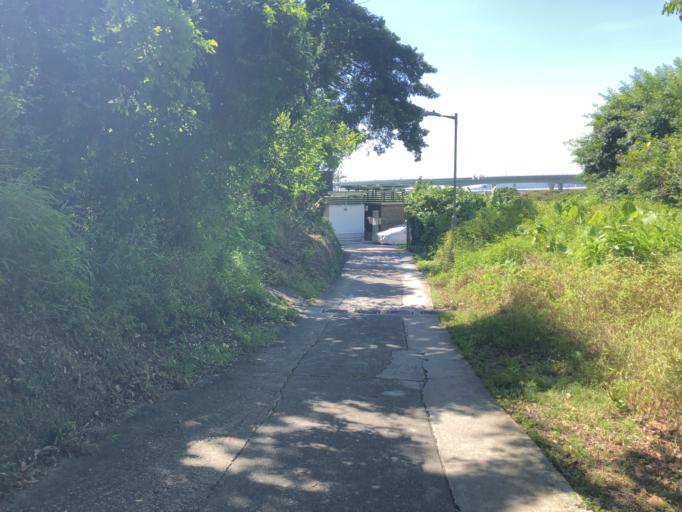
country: HK
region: Tuen Mun
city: Tuen Mun
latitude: 22.2954
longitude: 113.9722
